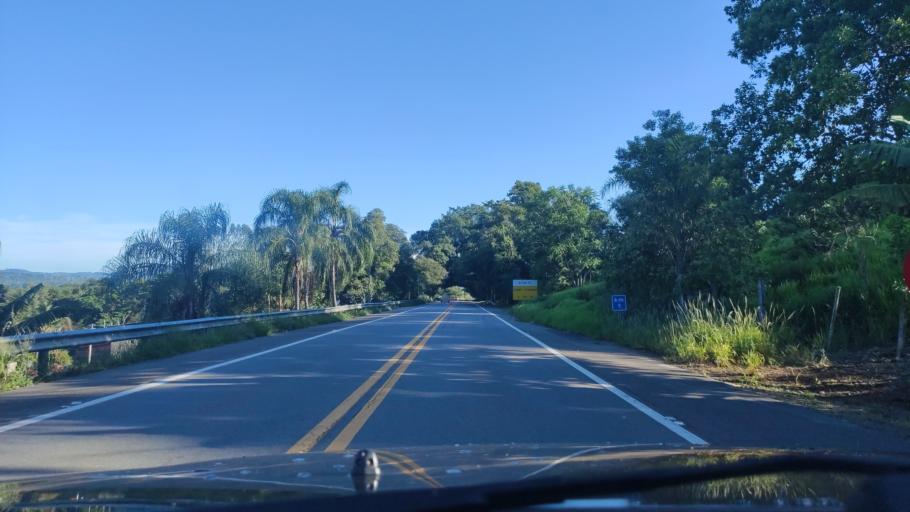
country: BR
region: Sao Paulo
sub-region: Socorro
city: Socorro
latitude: -22.5564
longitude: -46.5841
